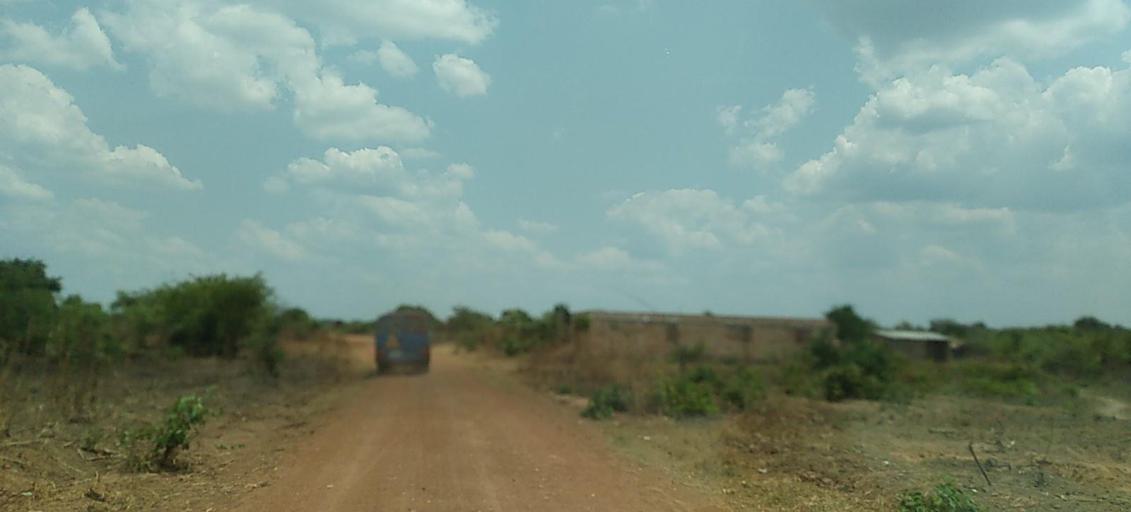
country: ZM
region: Copperbelt
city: Luanshya
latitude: -13.1277
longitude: 28.3110
